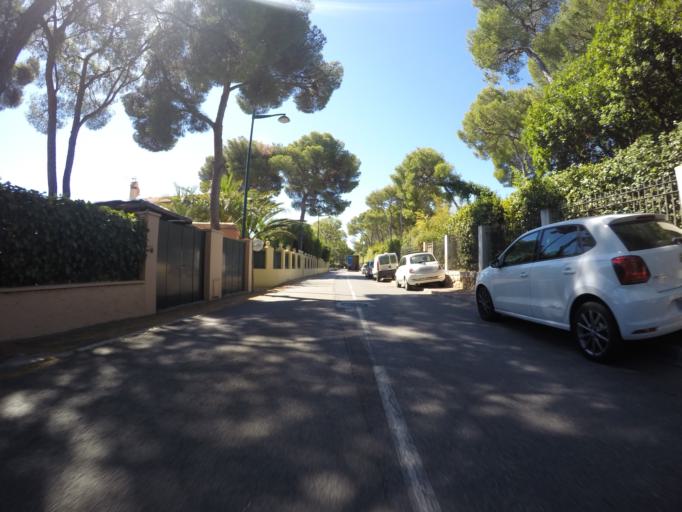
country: FR
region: Provence-Alpes-Cote d'Azur
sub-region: Departement des Alpes-Maritimes
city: Saint-Jean-Cap-Ferrat
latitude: 43.6817
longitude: 7.3334
